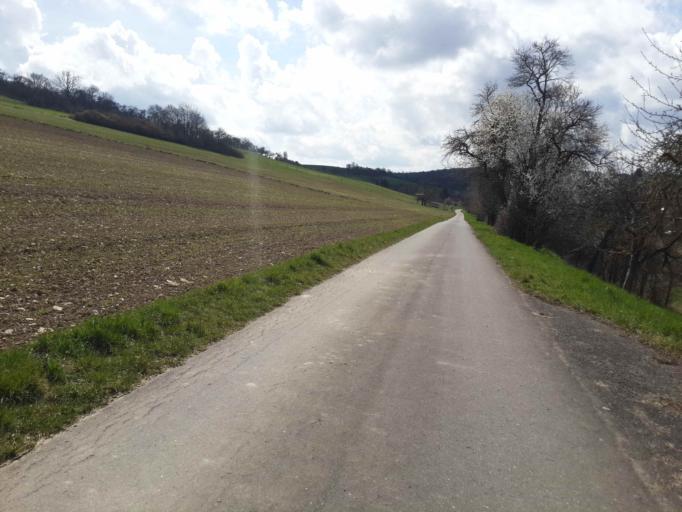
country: DE
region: Baden-Wuerttemberg
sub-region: Regierungsbezirk Stuttgart
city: Bad Mergentheim
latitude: 49.4481
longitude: 9.7559
